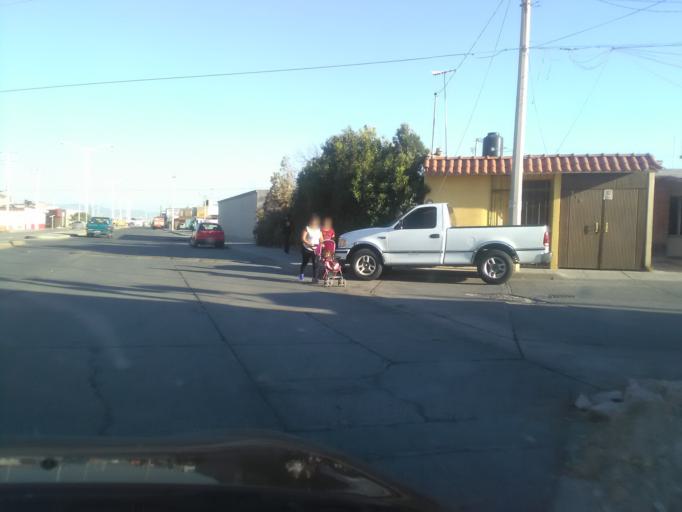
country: MX
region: Durango
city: Victoria de Durango
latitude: 24.0578
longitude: -104.5911
